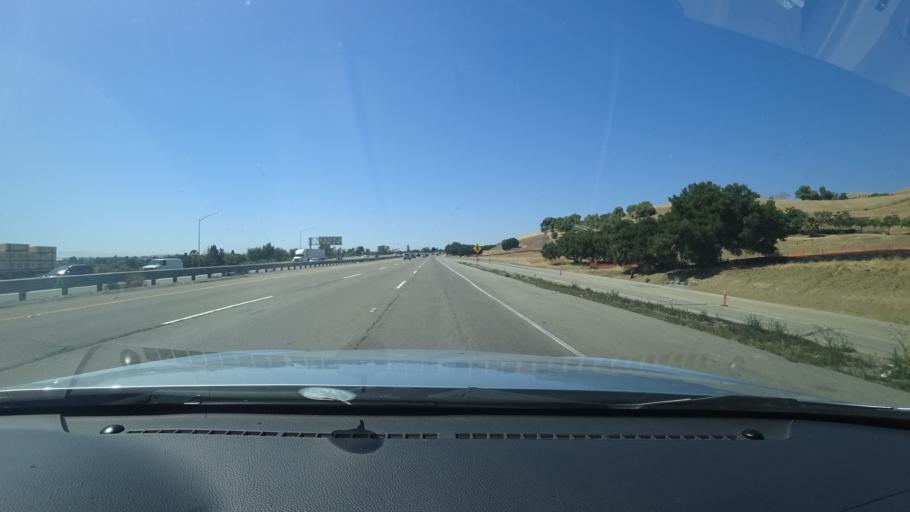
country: US
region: California
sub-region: Santa Clara County
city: Milpitas
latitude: 37.4686
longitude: -121.9071
